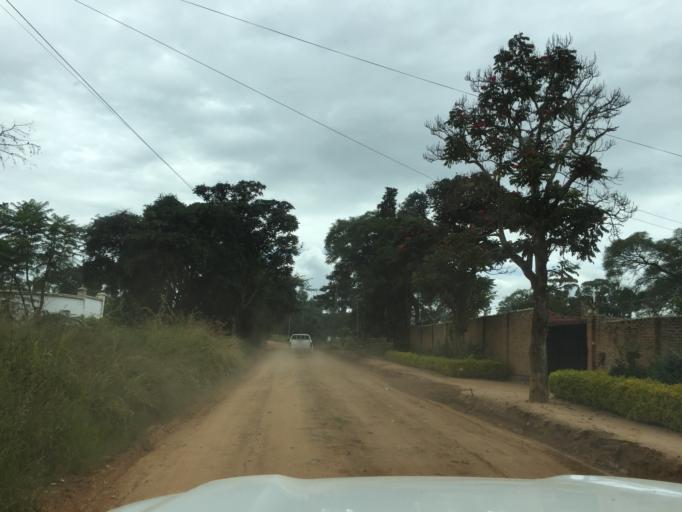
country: TZ
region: Iringa
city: Iringa
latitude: -7.7732
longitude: 35.7081
